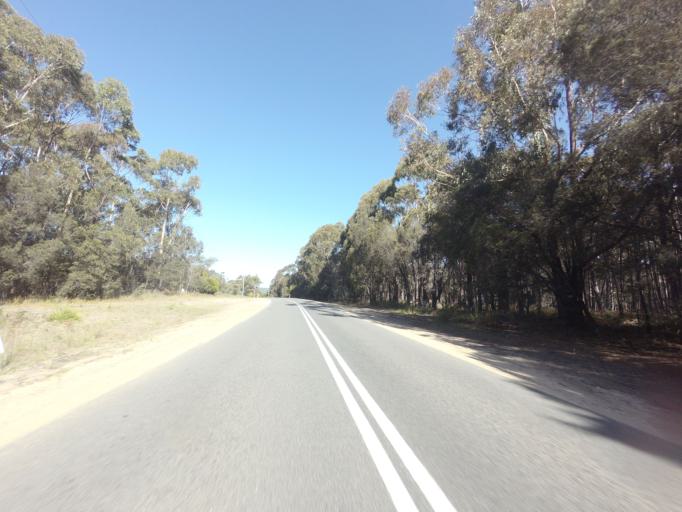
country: AU
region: Tasmania
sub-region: Break O'Day
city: St Helens
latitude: -41.6814
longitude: 148.2800
